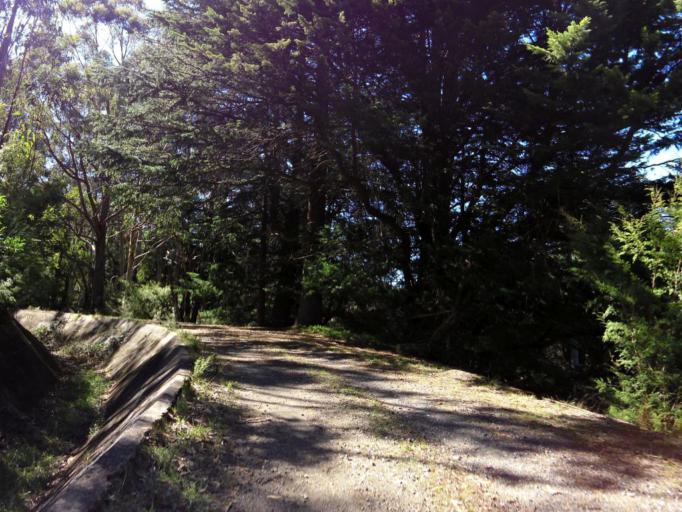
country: AU
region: Victoria
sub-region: Yarra Ranges
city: Launching Place
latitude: -37.7425
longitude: 145.5680
